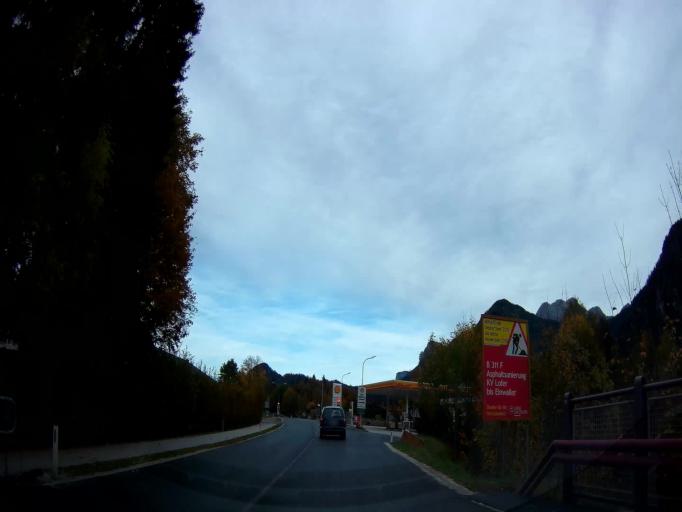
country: AT
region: Salzburg
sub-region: Politischer Bezirk Zell am See
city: Lofer
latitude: 47.5848
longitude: 12.6966
